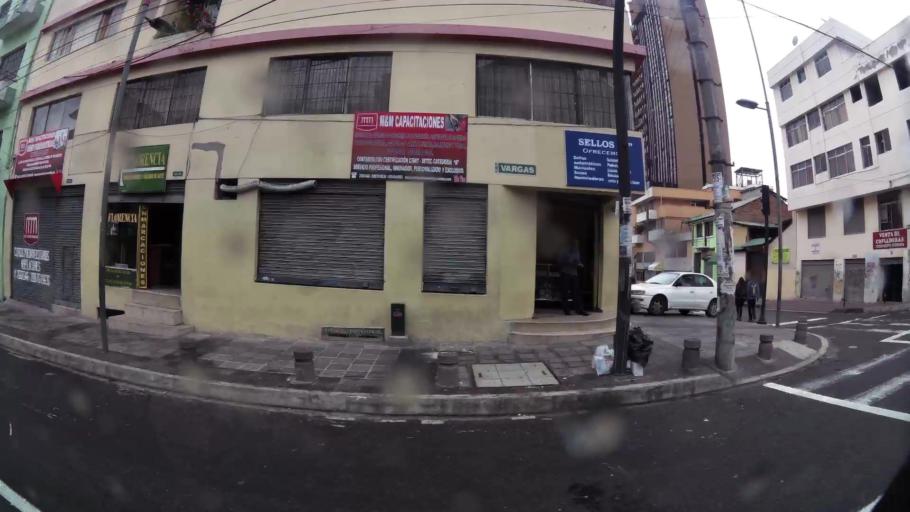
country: EC
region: Pichincha
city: Quito
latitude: -0.2125
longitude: -78.5045
